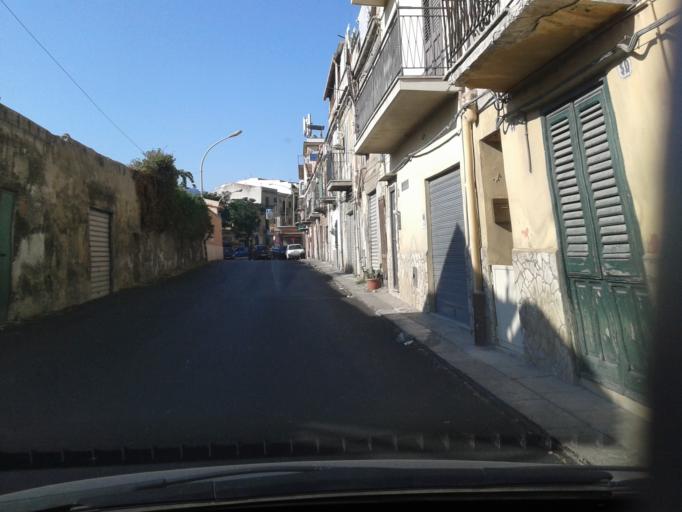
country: IT
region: Sicily
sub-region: Palermo
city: Monreale
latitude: 38.0952
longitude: 13.3092
